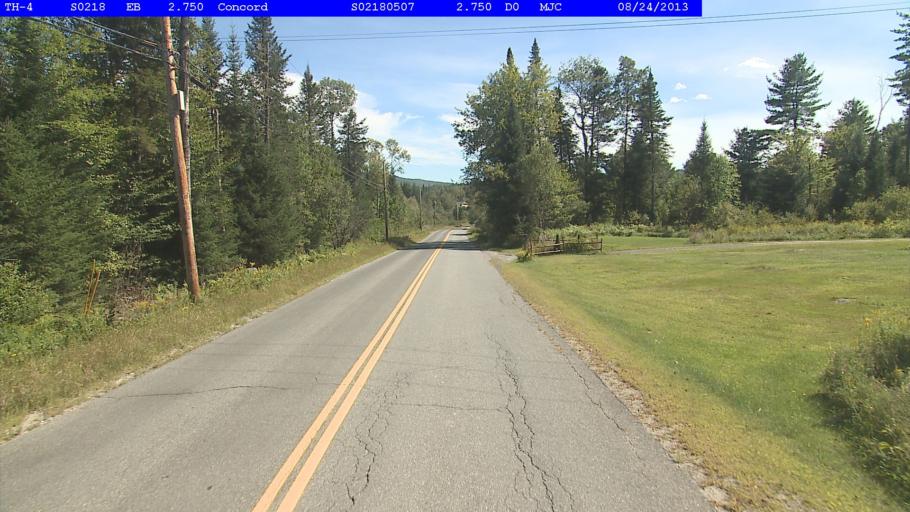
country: US
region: New Hampshire
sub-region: Grafton County
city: Littleton
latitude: 44.4293
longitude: -71.7527
